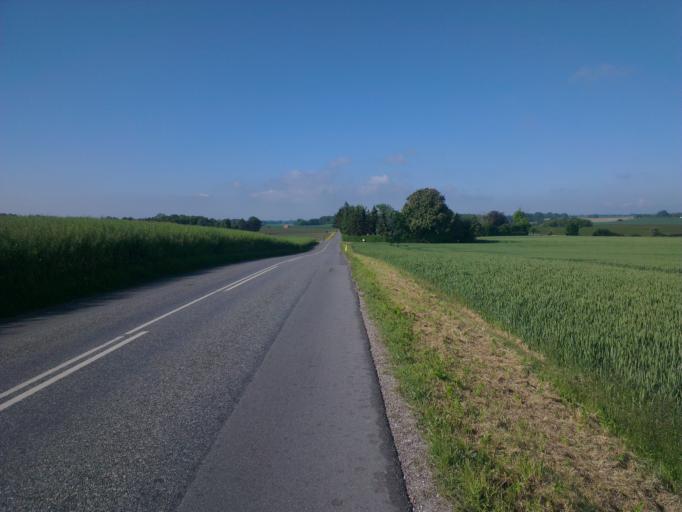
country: DK
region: Capital Region
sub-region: Frederikssund Kommune
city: Frederikssund
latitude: 55.7966
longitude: 12.0162
